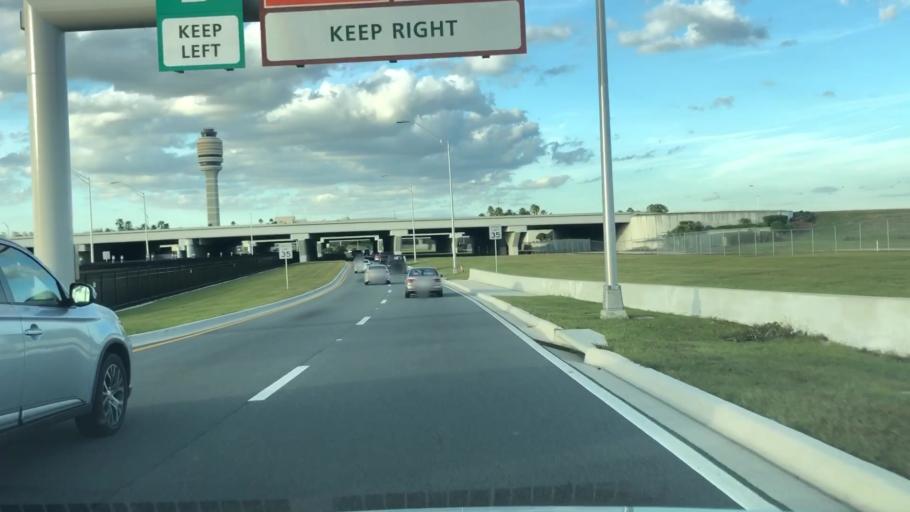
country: US
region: Florida
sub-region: Orange County
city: Taft
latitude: 28.4209
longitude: -81.3062
